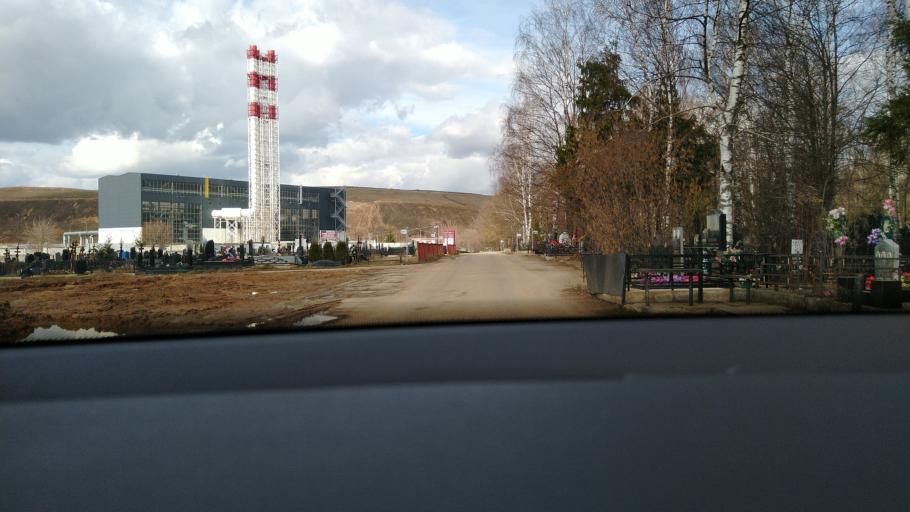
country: RU
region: Moskovskaya
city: Mosrentgen
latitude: 55.6055
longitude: 37.4340
